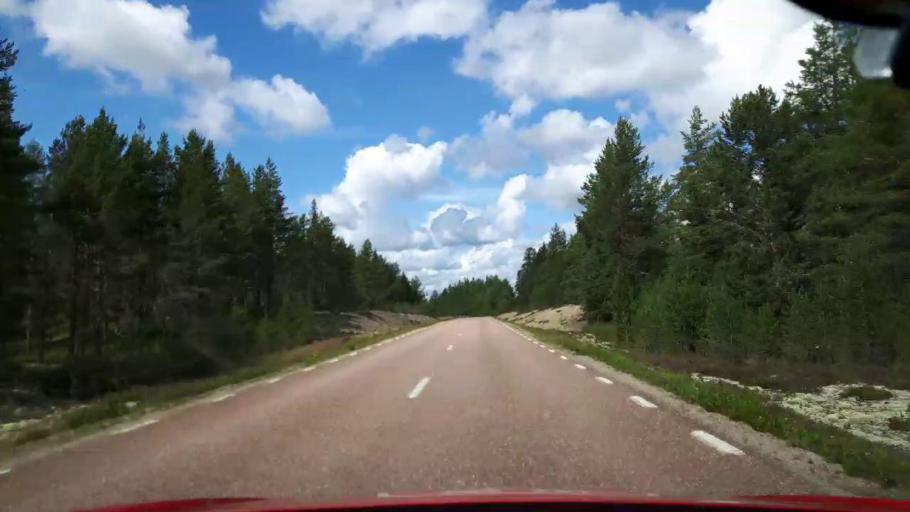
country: SE
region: Dalarna
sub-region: Alvdalens Kommun
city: AElvdalen
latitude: 61.8040
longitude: 13.6563
